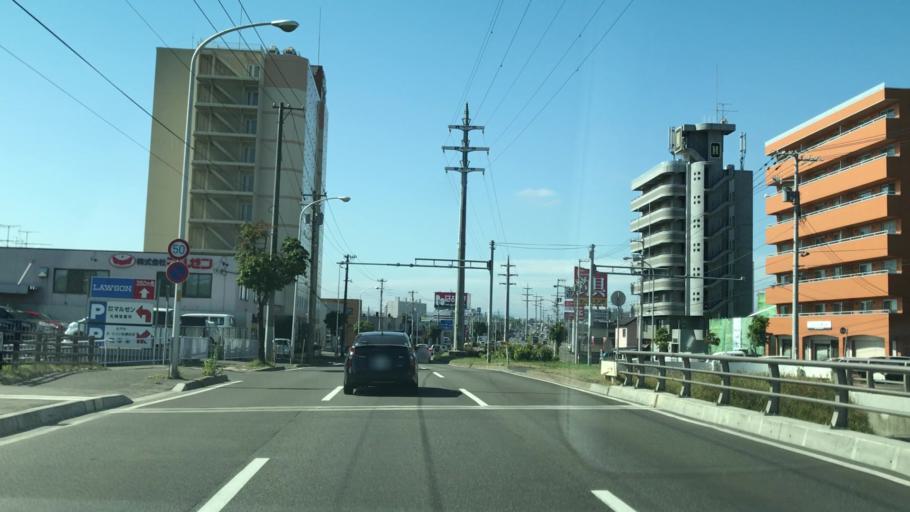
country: JP
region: Hokkaido
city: Sapporo
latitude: 43.0659
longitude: 141.4085
